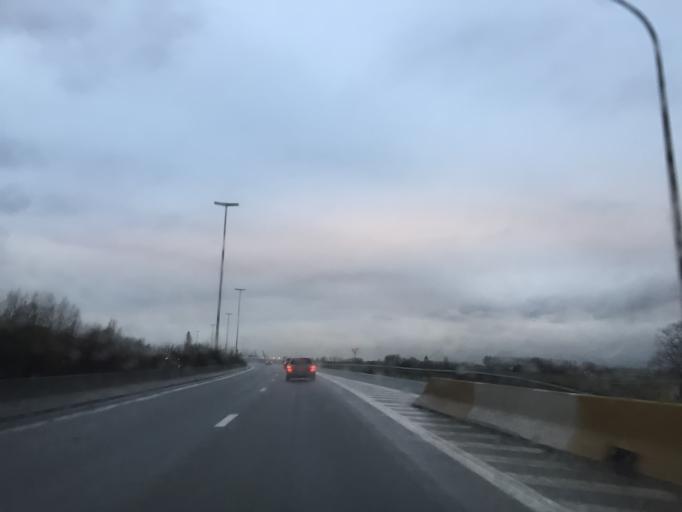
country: BE
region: Flanders
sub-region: Provincie Antwerpen
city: Kapellen
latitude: 51.2942
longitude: 4.4044
